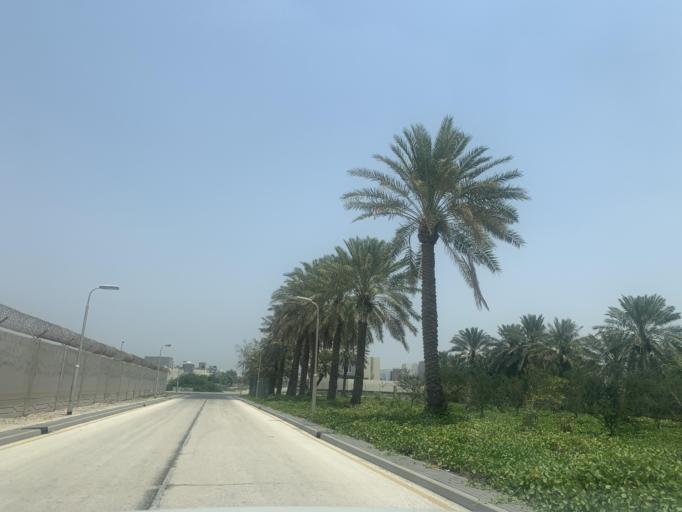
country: BH
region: Central Governorate
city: Madinat Hamad
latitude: 26.1402
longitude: 50.4588
